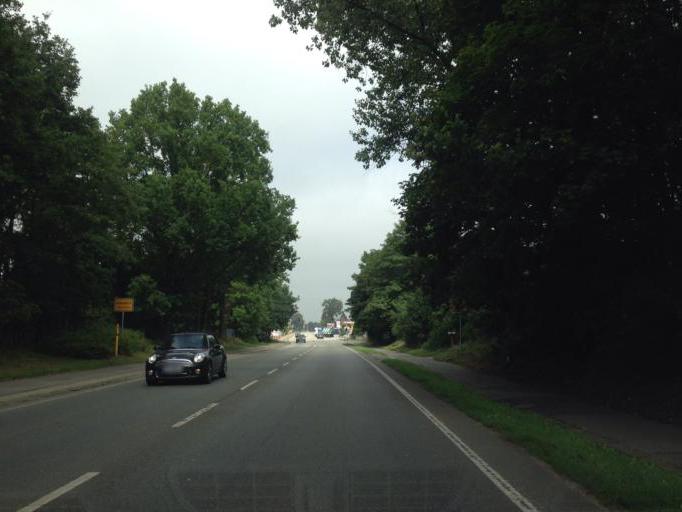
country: DE
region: Lower Saxony
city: Adendorf
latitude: 53.2826
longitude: 10.4272
